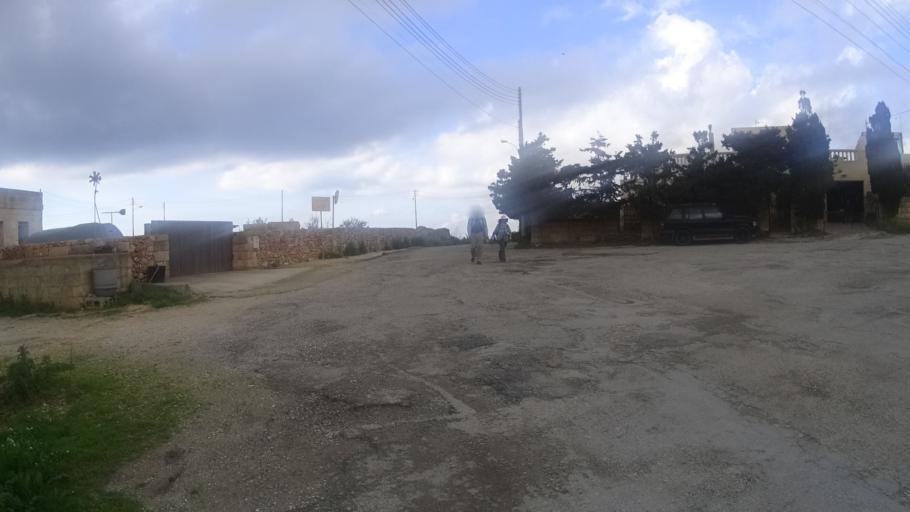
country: MT
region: L-Imgarr
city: Imgarr
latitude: 35.8973
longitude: 14.3655
